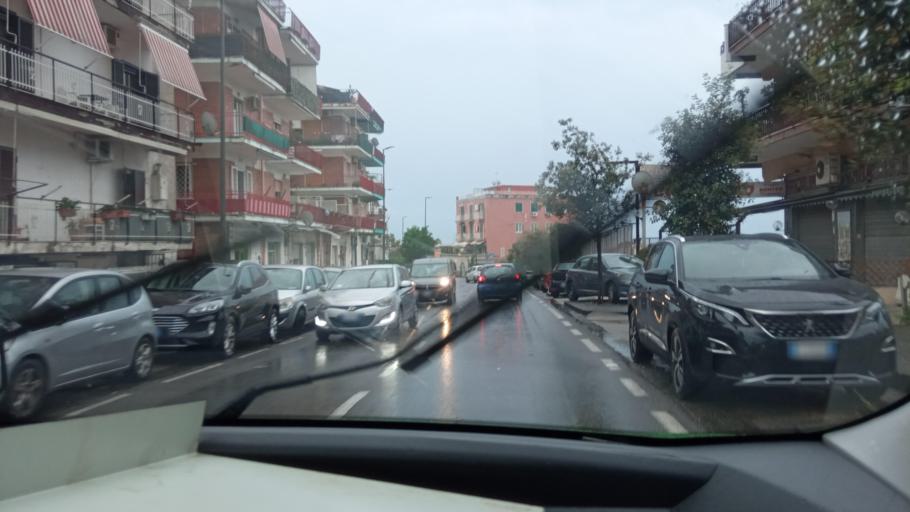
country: IT
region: Campania
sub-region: Provincia di Napoli
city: Pozzuoli
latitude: 40.8327
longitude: 14.1163
